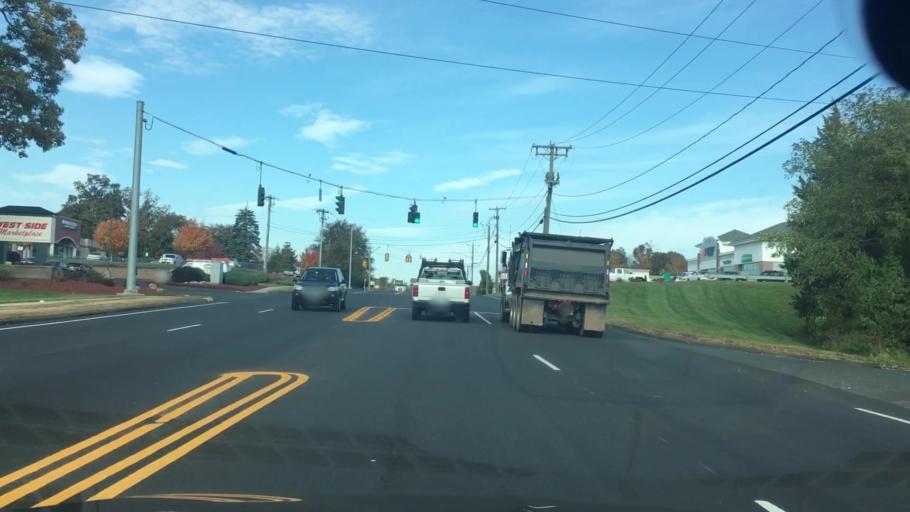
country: US
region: Connecticut
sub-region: Middlesex County
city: Cromwell
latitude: 41.6459
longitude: -72.6779
